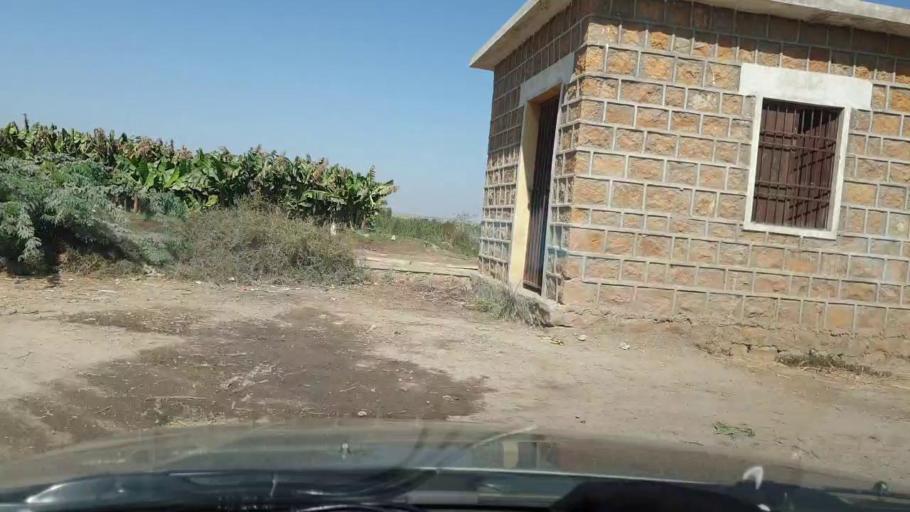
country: PK
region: Sindh
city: Thatta
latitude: 24.6408
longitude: 67.8927
